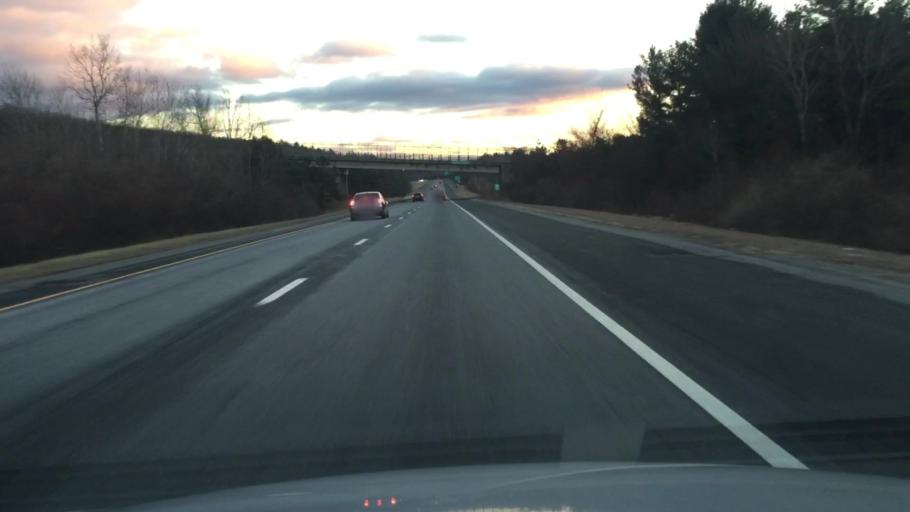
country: US
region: Massachusetts
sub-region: Worcester County
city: West Boylston
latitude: 42.3611
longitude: -71.8144
